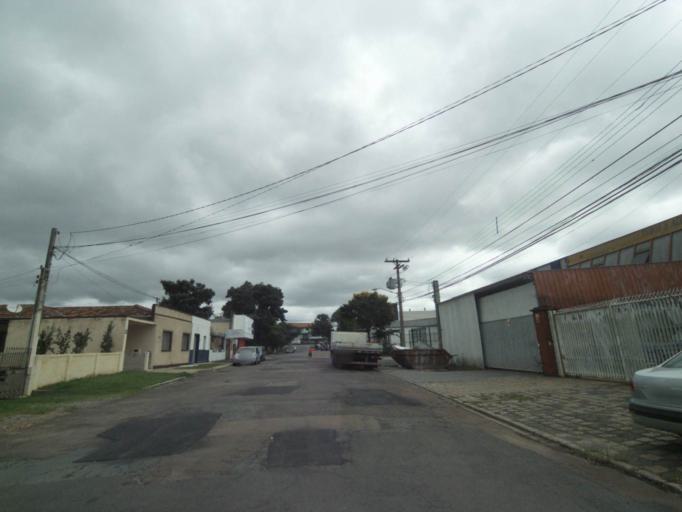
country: BR
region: Parana
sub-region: Curitiba
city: Curitiba
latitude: -25.4941
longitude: -49.2761
